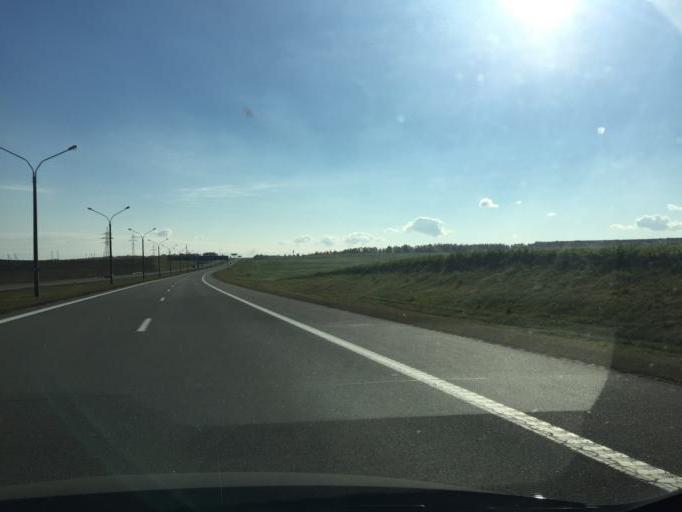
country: BY
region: Minsk
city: Slabada
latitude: 54.0054
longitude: 27.9064
